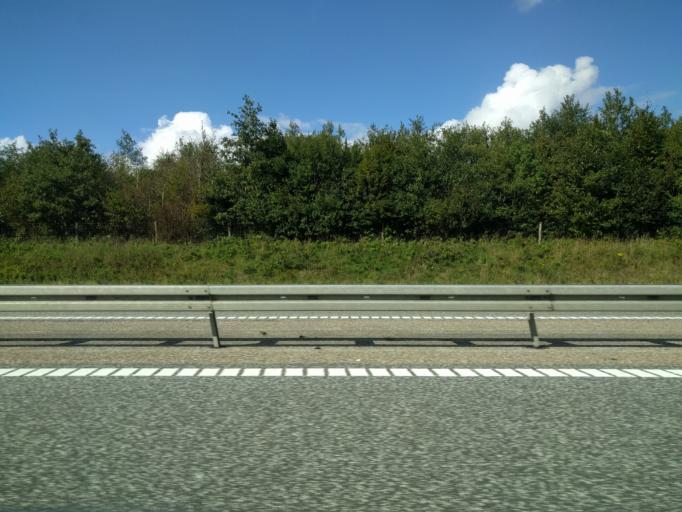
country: DK
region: Central Jutland
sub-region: Hedensted Kommune
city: Torring
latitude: 55.8375
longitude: 9.4311
